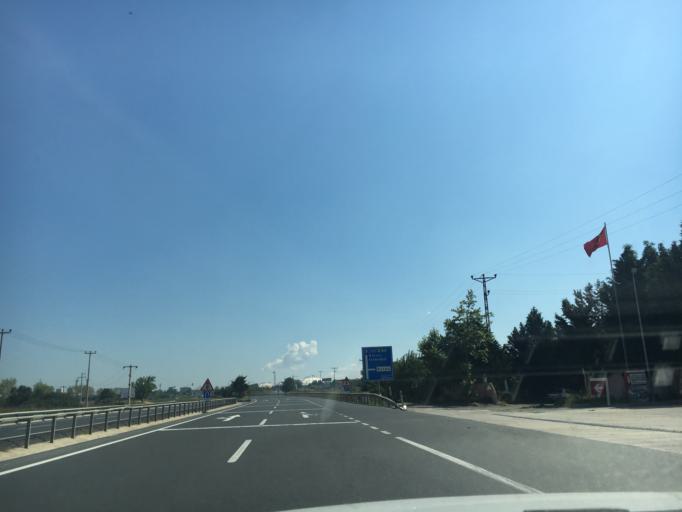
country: TR
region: Tekirdag
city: Marmara Ereglisi
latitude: 40.9859
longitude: 27.9688
